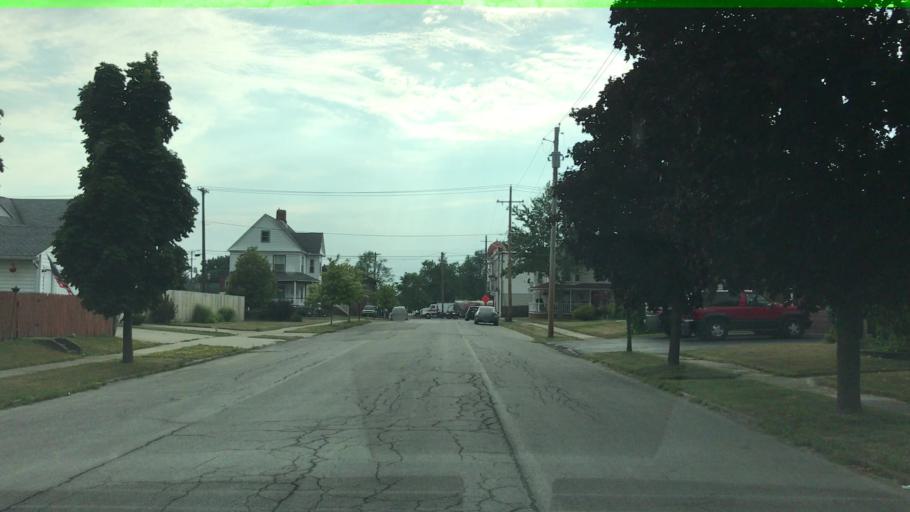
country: US
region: New York
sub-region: Erie County
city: Depew
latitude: 42.9139
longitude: -78.6949
